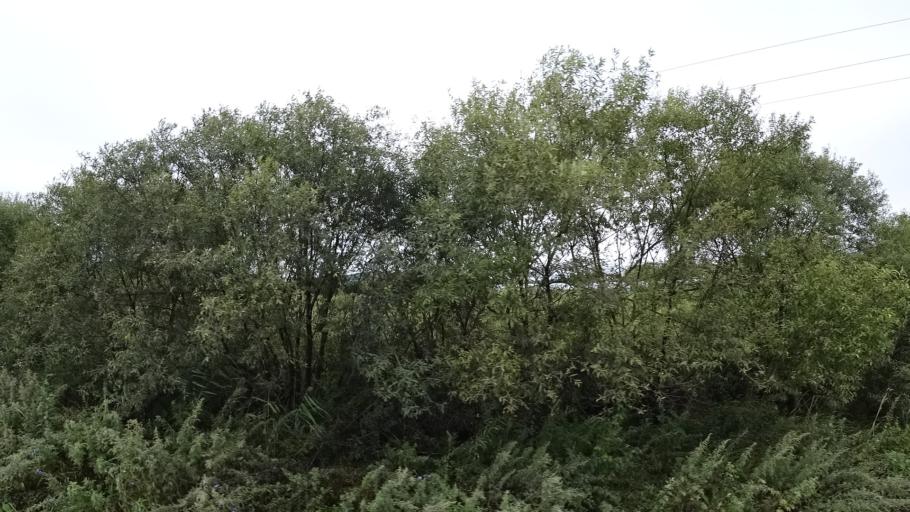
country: RU
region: Primorskiy
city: Monastyrishche
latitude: 44.1842
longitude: 132.4831
